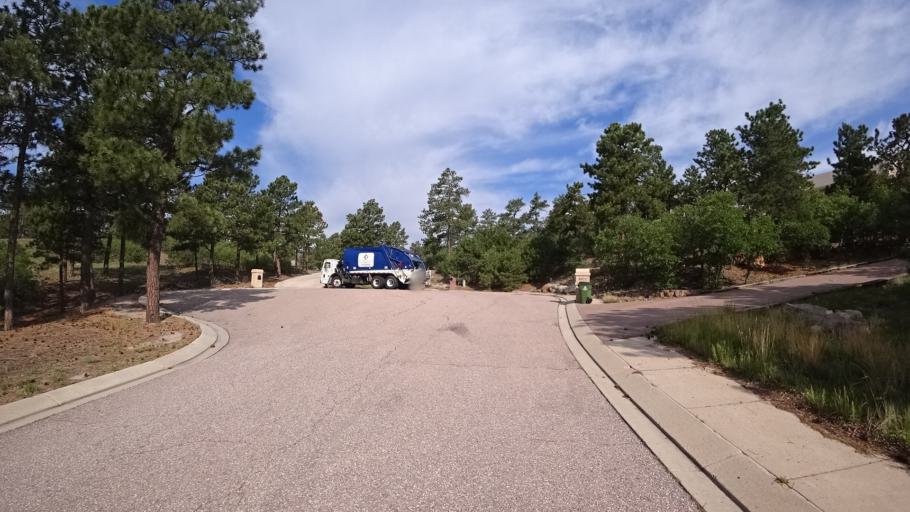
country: US
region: Colorado
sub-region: El Paso County
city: Air Force Academy
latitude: 38.9405
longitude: -104.8305
